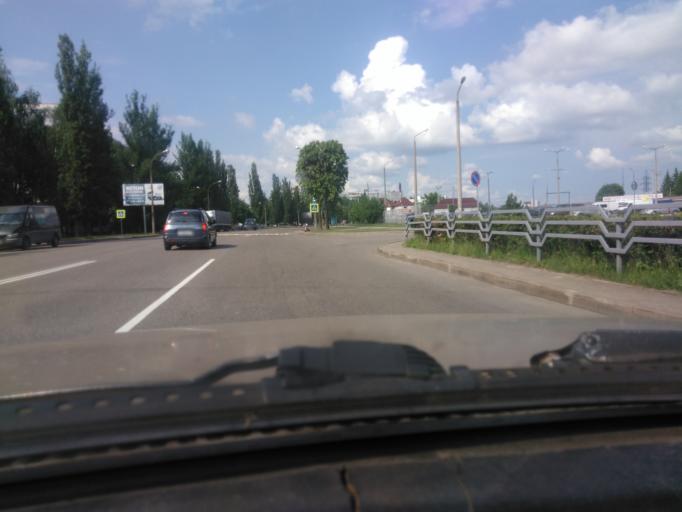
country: BY
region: Mogilev
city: Mahilyow
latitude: 53.9289
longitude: 30.3623
